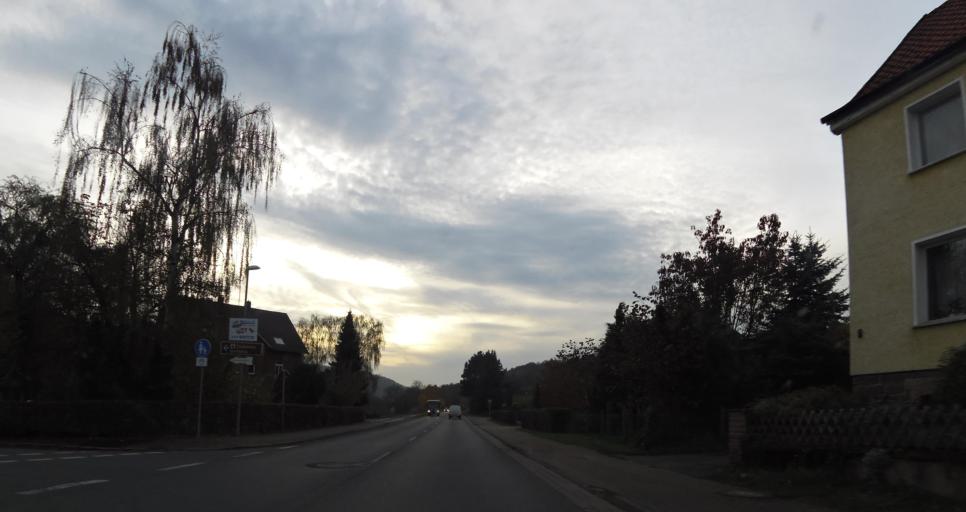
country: DE
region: Lower Saxony
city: Halle
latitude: 51.9899
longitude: 9.5571
